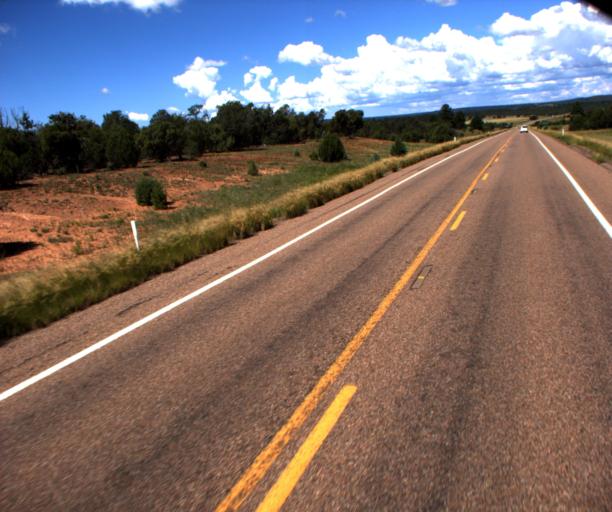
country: US
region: Arizona
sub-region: Navajo County
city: Linden
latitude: 34.3452
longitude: -110.2944
